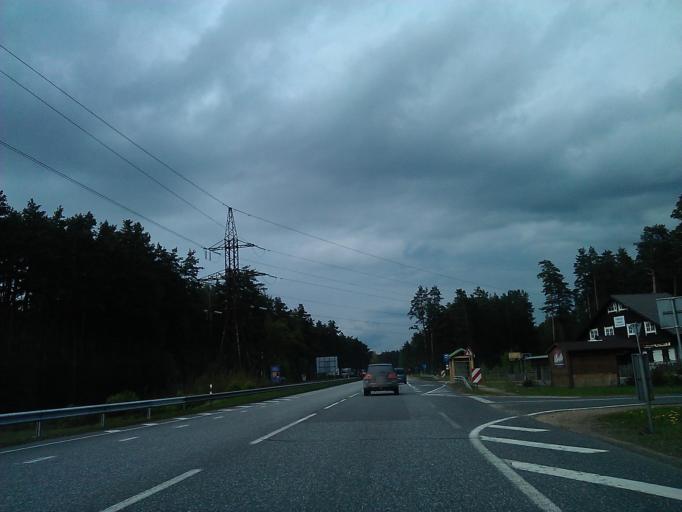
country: LV
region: Riga
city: Bergi
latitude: 57.0190
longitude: 24.3126
